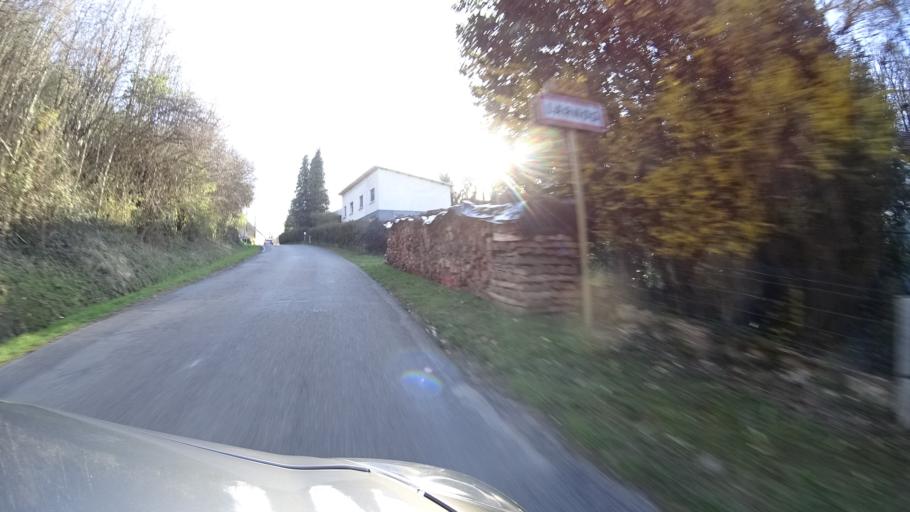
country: FR
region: Franche-Comte
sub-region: Departement du Doubs
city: Avanne-Aveney
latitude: 47.1943
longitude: 5.9857
